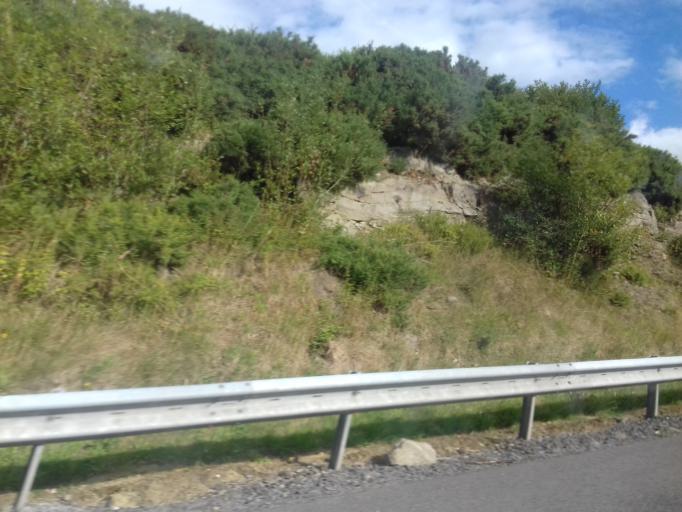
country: IE
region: Leinster
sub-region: Kilkenny
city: Thomastown
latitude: 52.4630
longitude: -7.2375
